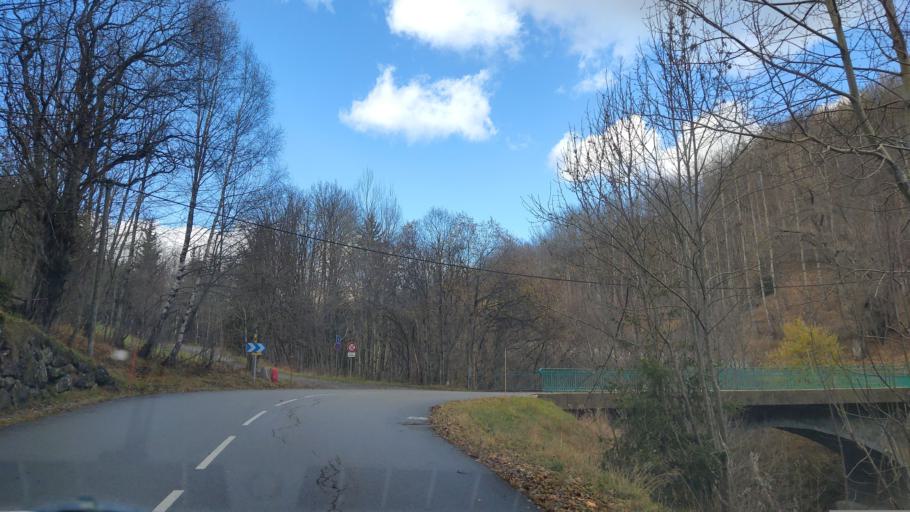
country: FR
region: Rhone-Alpes
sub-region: Departement de la Savoie
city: Saint-Jean-de-Maurienne
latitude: 45.1958
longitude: 6.2820
